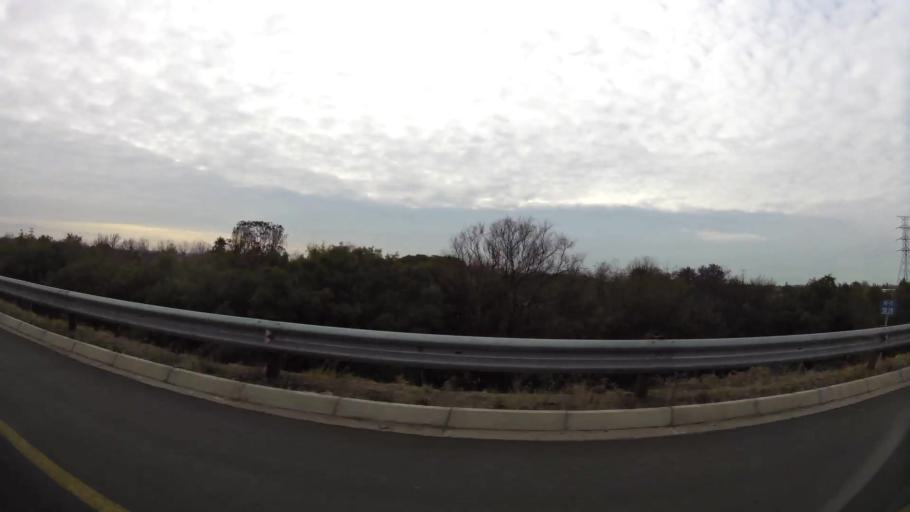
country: ZA
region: Orange Free State
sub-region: Mangaung Metropolitan Municipality
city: Bloemfontein
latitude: -29.1328
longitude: 26.1657
